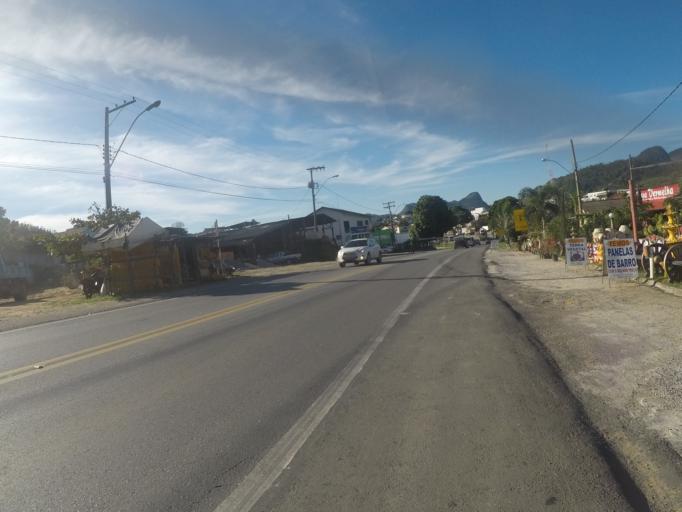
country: BR
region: Espirito Santo
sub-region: Fundao
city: Fundao
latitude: -19.9359
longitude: -40.4062
